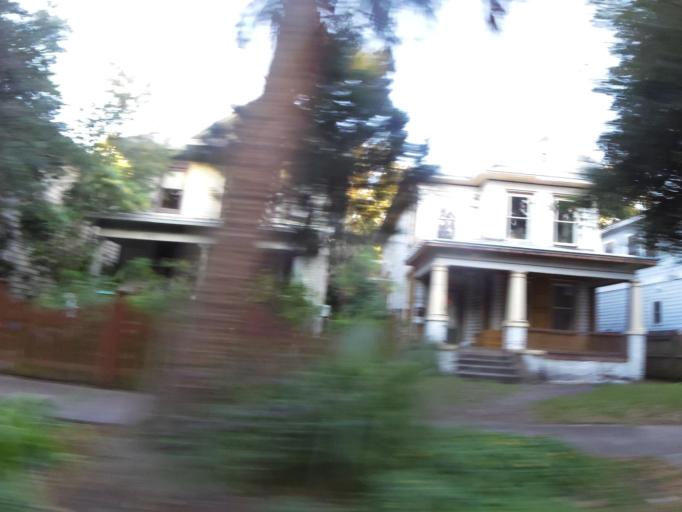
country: US
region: Florida
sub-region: Duval County
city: Jacksonville
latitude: 30.3472
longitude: -81.6491
